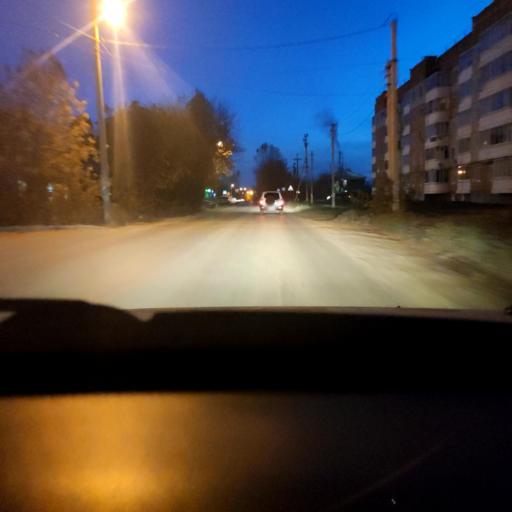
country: RU
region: Perm
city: Ferma
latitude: 57.8977
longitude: 56.3015
